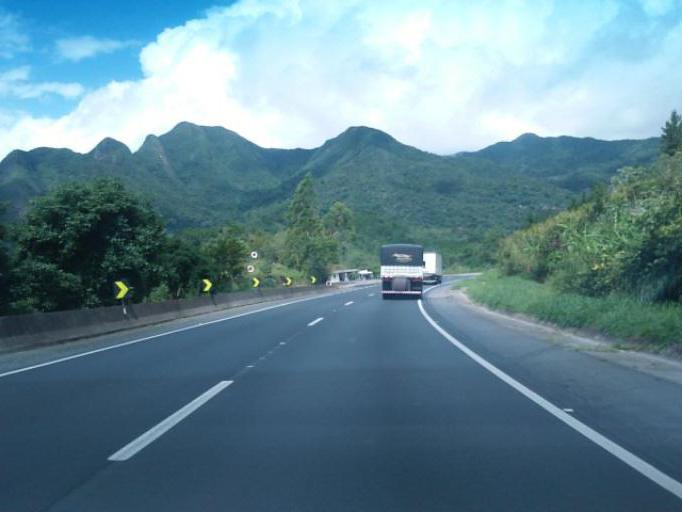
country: BR
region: Sao Paulo
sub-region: Cajati
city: Cajati
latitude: -24.8798
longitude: -48.2197
